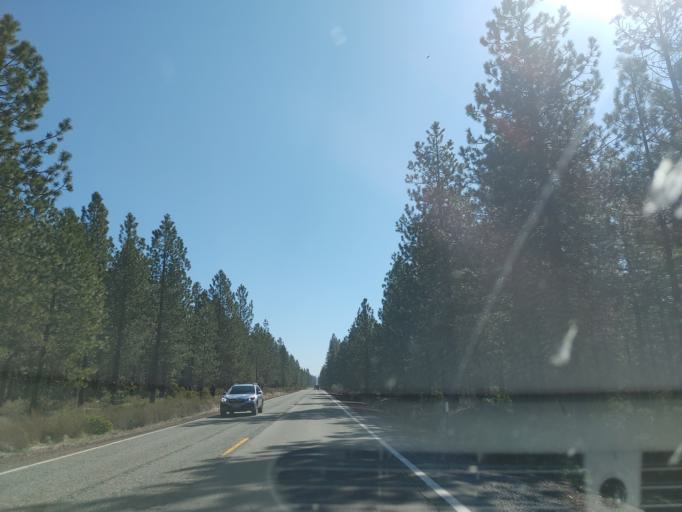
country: US
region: California
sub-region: Siskiyou County
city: McCloud
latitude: 41.2527
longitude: -122.0995
